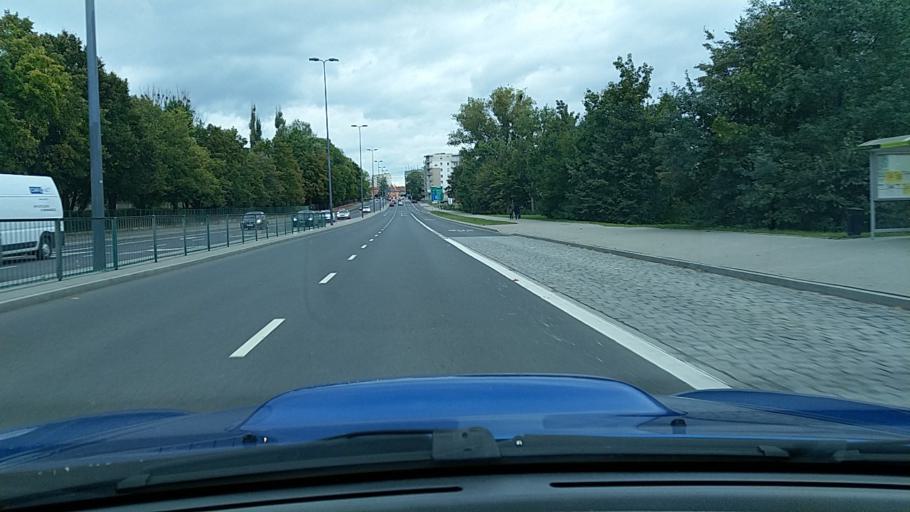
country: PL
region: Warmian-Masurian Voivodeship
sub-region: Olsztyn
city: Kortowo
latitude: 53.7616
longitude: 20.4631
